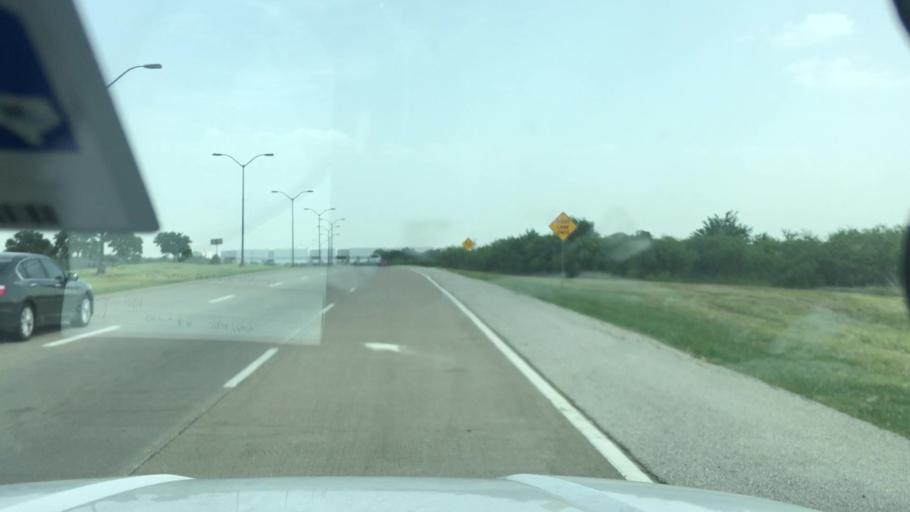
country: US
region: Texas
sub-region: Tarrant County
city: Euless
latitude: 32.8663
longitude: -97.0536
